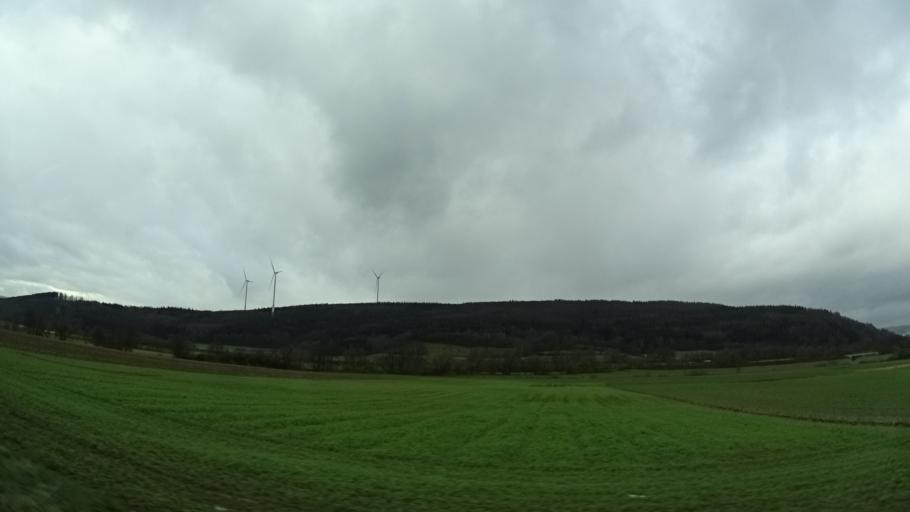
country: DE
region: Hesse
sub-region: Regierungsbezirk Darmstadt
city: Bad Soden-Salmunster
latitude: 50.2630
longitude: 9.3568
